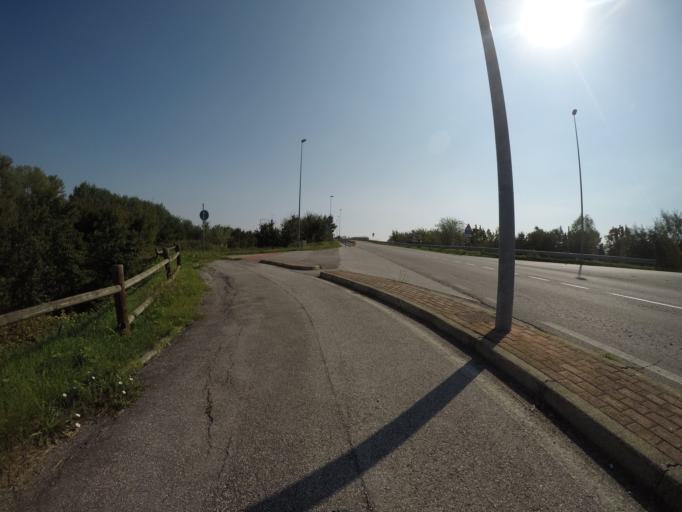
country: IT
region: Veneto
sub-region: Provincia di Rovigo
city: Polesella
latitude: 44.9573
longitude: 11.7339
